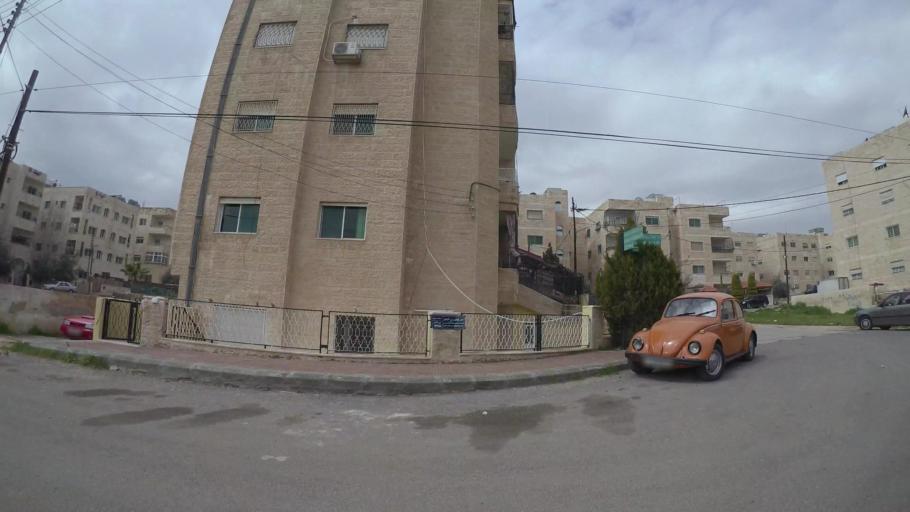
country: JO
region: Amman
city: Amman
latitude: 31.9887
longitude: 35.9271
